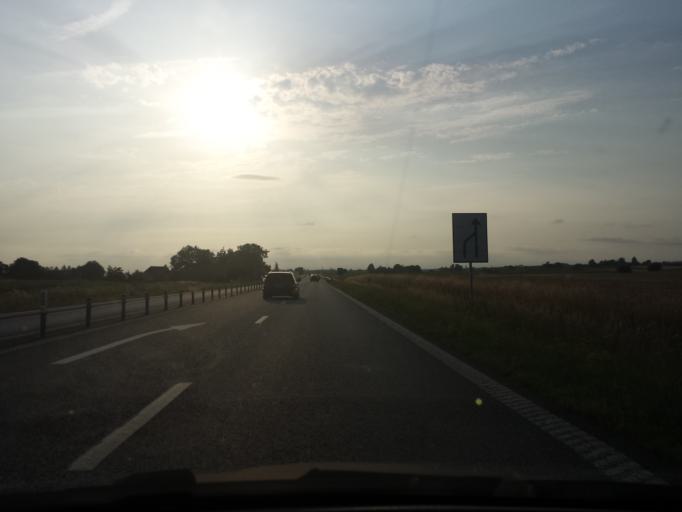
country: SE
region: Skane
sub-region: Skurups Kommun
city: Rydsgard
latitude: 55.4781
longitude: 13.6339
